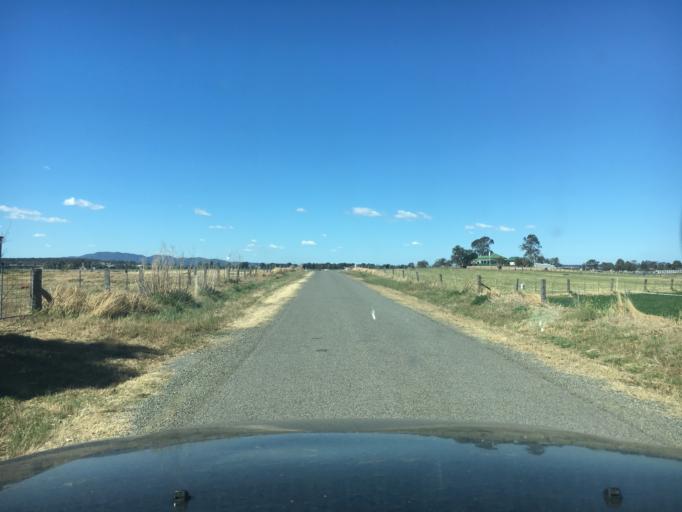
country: AU
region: New South Wales
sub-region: Singleton
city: Singleton
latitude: -32.5817
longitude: 151.1888
